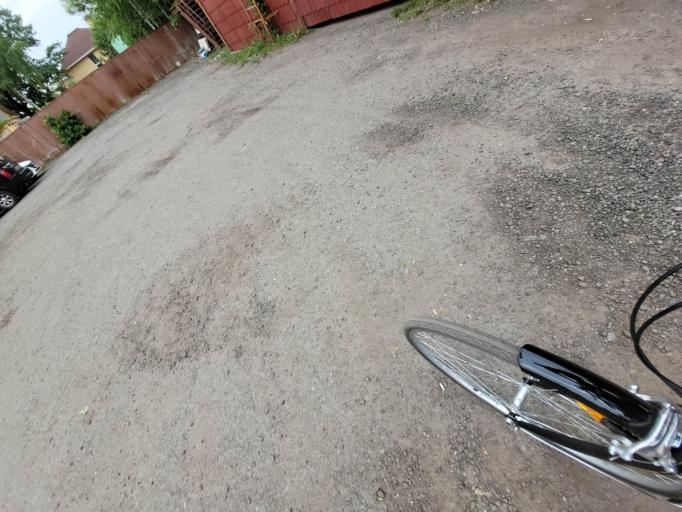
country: RU
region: Moskovskaya
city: Yubileyny
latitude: 55.9346
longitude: 37.8613
